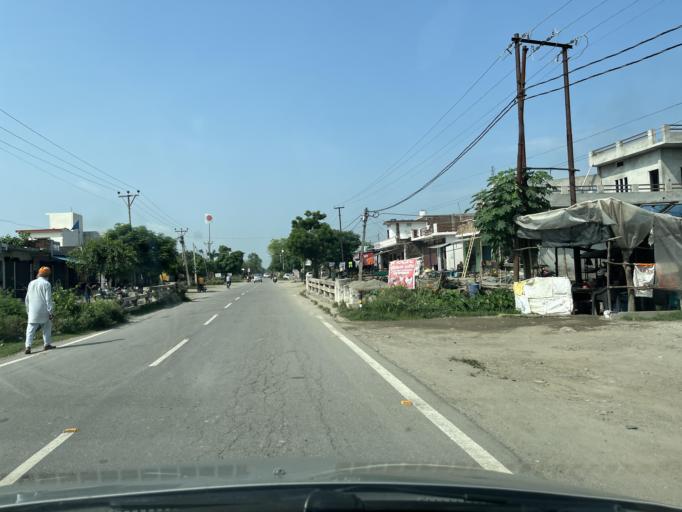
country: IN
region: Uttarakhand
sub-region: Udham Singh Nagar
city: Bazpur
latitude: 29.2090
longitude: 79.2140
